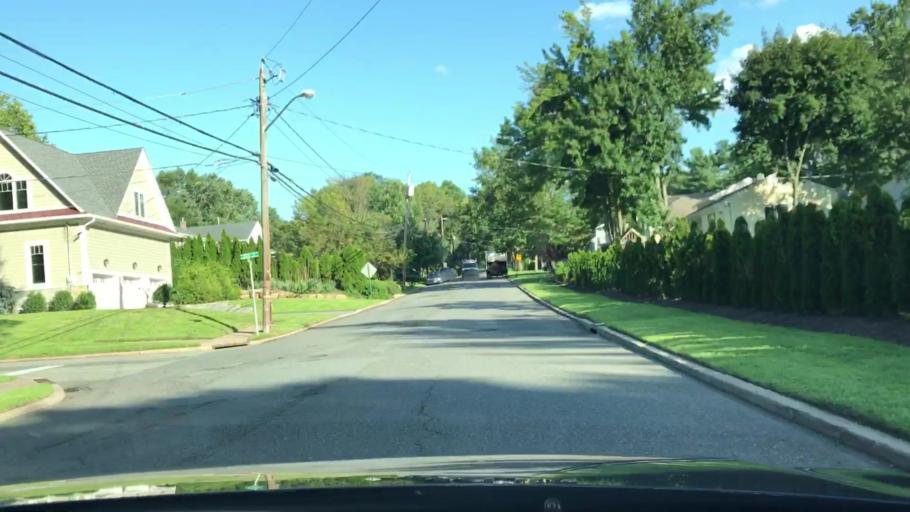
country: US
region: New Jersey
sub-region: Bergen County
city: Cresskill
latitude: 40.9384
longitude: -73.9571
